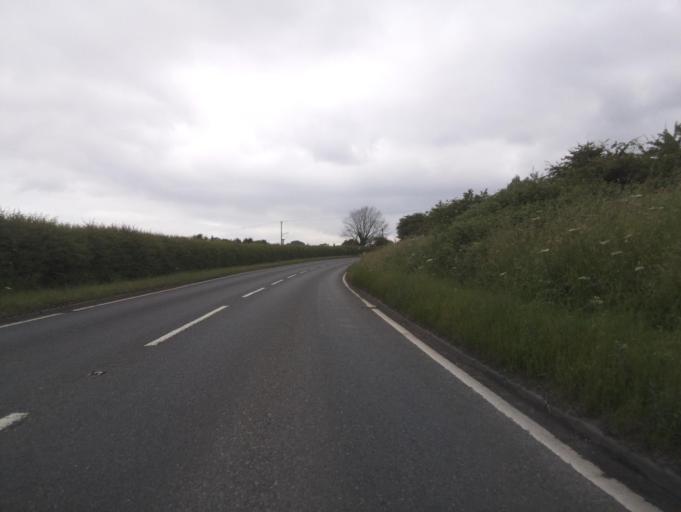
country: GB
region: England
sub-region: Staffordshire
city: Mayfield
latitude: 53.0053
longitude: -1.7491
